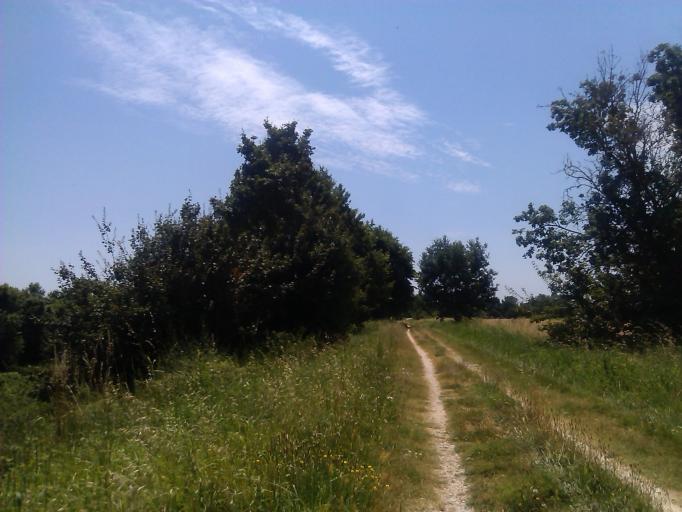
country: IT
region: Tuscany
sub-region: Province of Arezzo
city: Cesa
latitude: 43.3233
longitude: 11.8342
